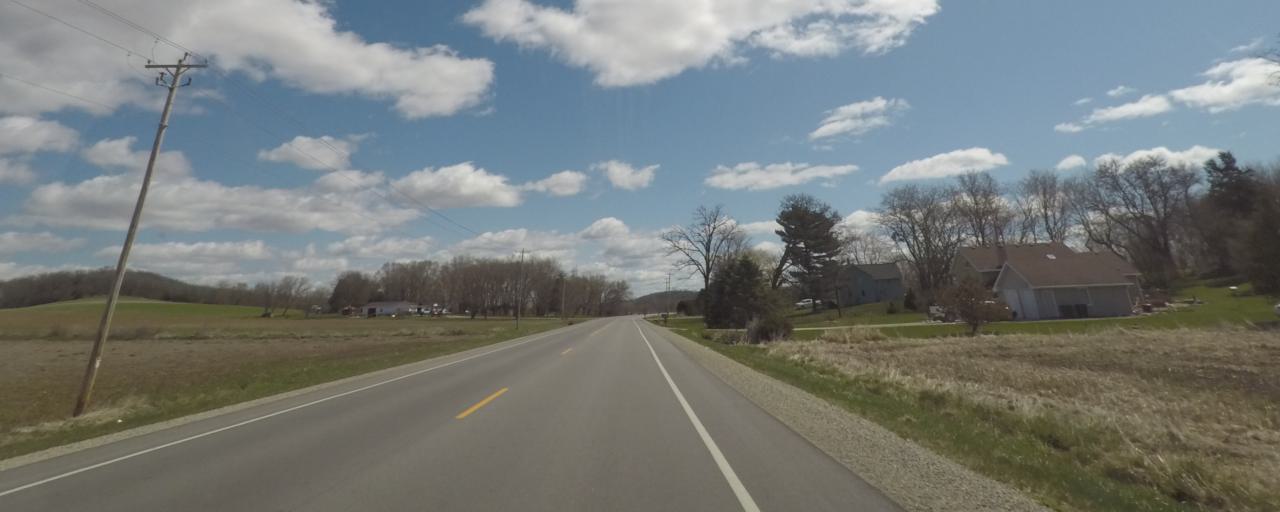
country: US
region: Wisconsin
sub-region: Jefferson County
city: Lake Mills
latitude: 43.0875
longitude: -88.9814
